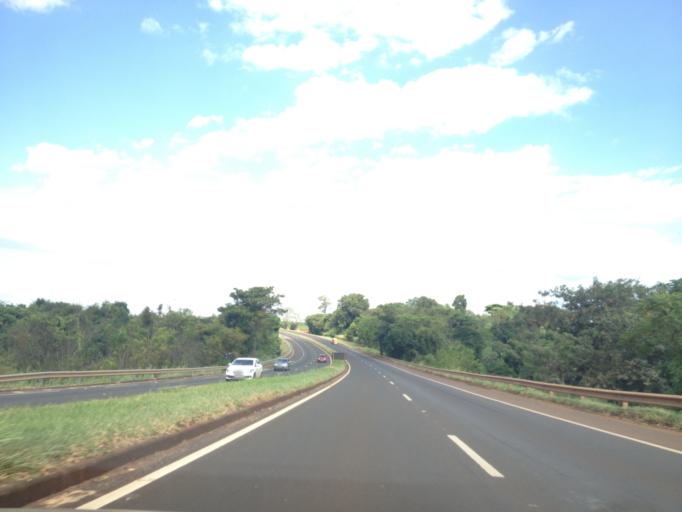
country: BR
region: Parana
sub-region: Marialva
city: Marialva
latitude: -23.4881
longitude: -51.8186
